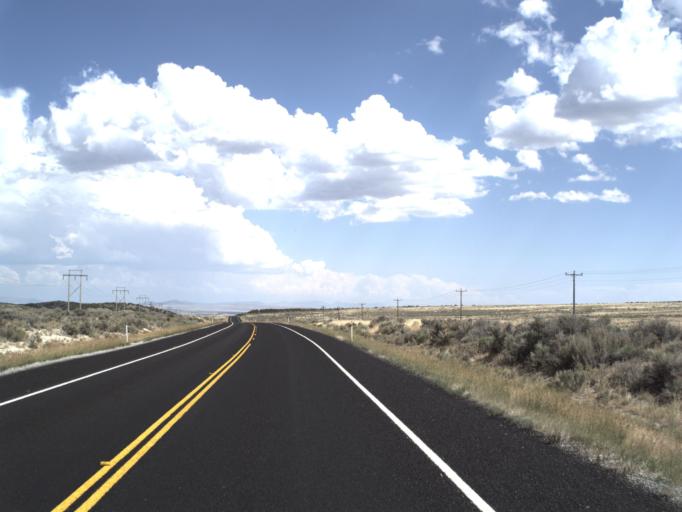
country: US
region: Idaho
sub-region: Minidoka County
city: Rupert
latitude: 41.9931
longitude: -113.1876
